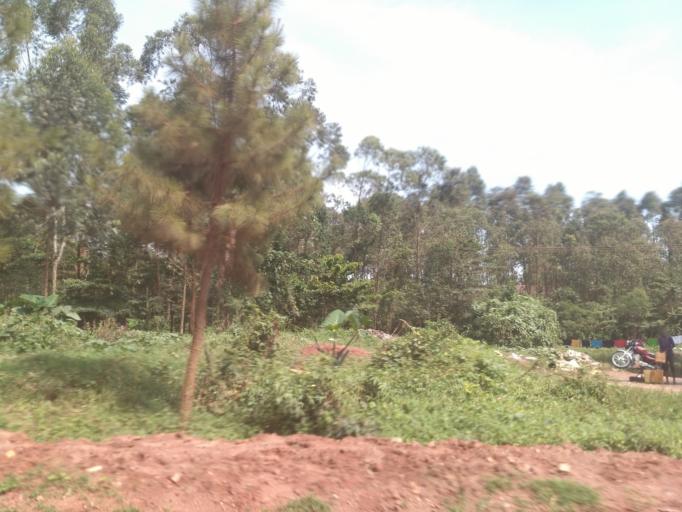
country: UG
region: Central Region
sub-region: Wakiso District
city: Kireka
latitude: 0.4411
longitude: 32.5910
